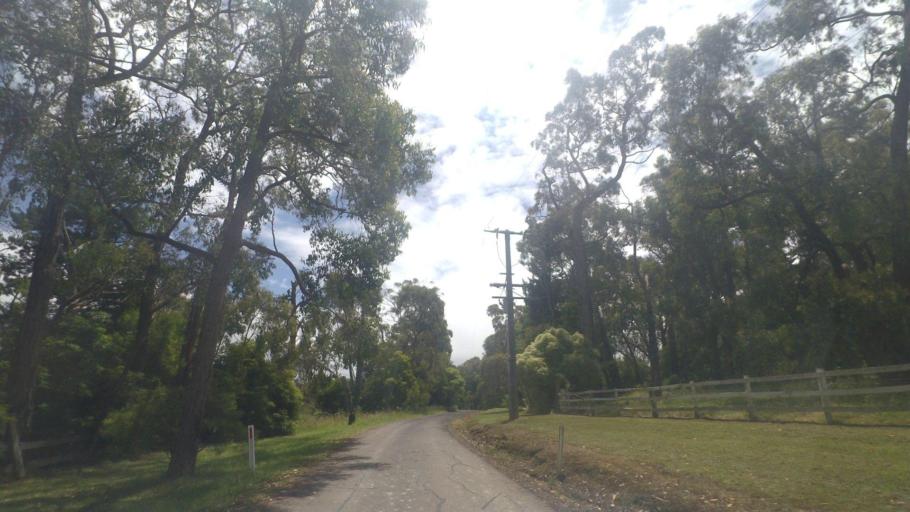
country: AU
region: Victoria
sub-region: Yarra Ranges
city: Mount Evelyn
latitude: -37.7763
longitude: 145.3748
